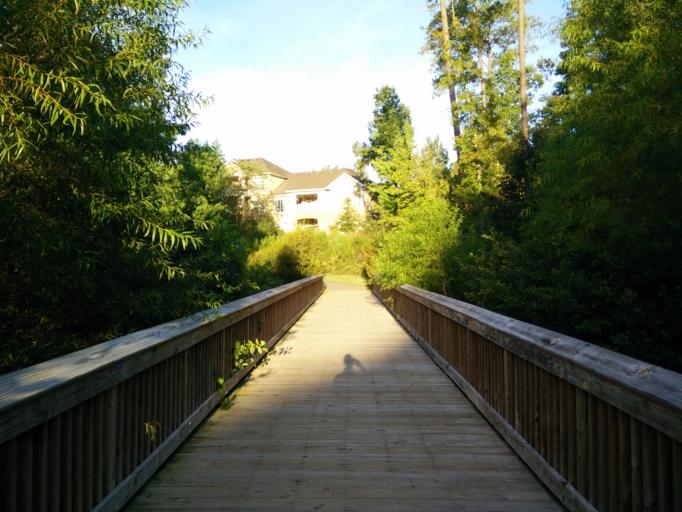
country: US
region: North Carolina
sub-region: Wake County
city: Cary
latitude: 35.7499
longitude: -78.7484
